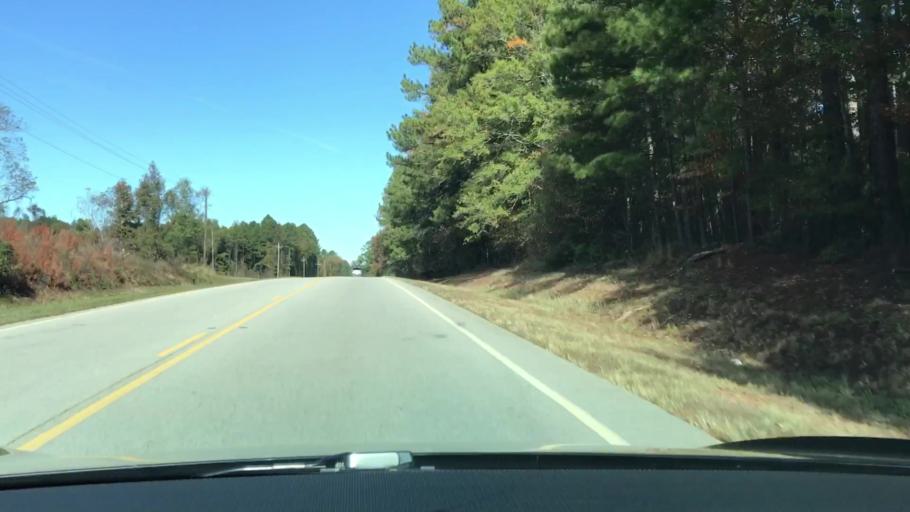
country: US
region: Georgia
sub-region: Warren County
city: Firing Range
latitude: 33.4336
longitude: -82.6876
